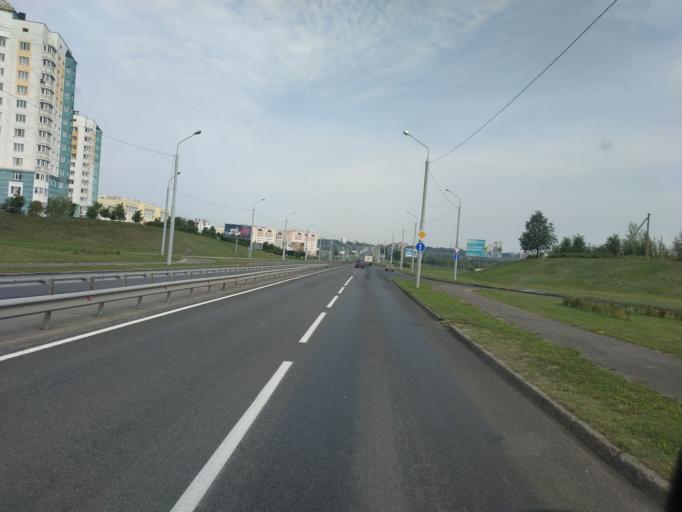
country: BY
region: Mogilev
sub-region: Mahilyowski Rayon
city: Veyno
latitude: 53.8792
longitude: 30.3835
